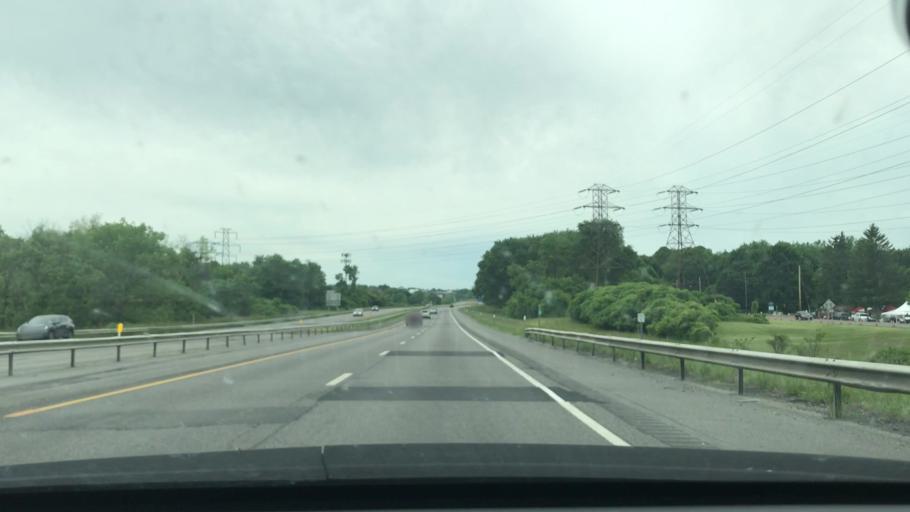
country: US
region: New York
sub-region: Onondaga County
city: Lakeland
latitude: 43.1157
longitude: -76.2462
